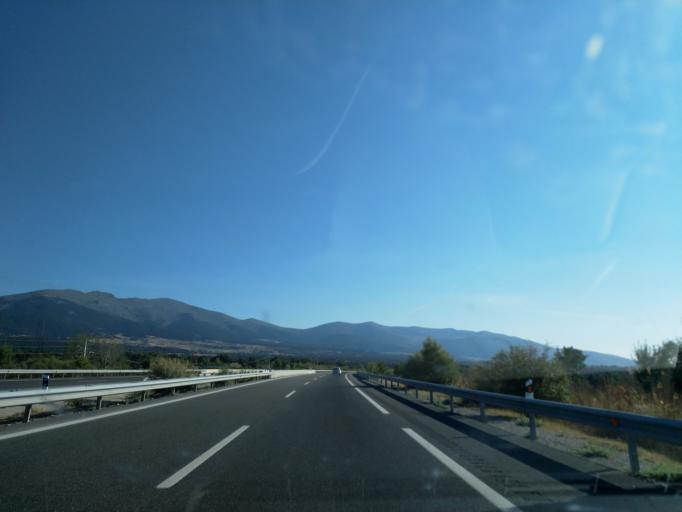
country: ES
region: Castille and Leon
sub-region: Provincia de Segovia
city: Segovia
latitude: 40.8823
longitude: -4.1176
